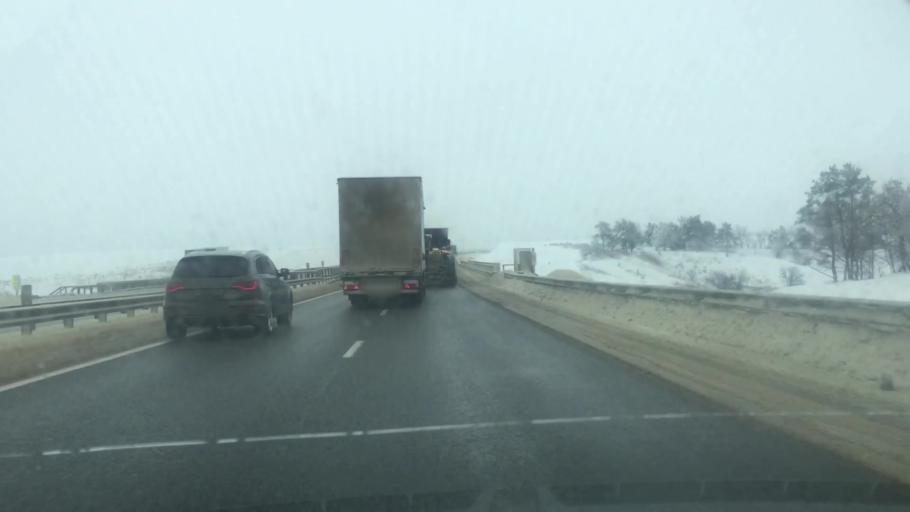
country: RU
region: Lipetsk
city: Stanovoye
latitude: 52.7897
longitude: 38.3616
